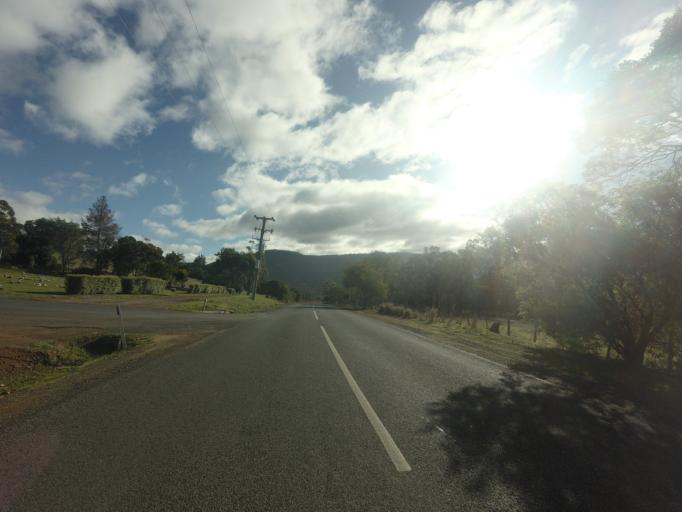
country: AU
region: Tasmania
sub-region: Derwent Valley
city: New Norfolk
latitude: -42.7860
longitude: 147.1185
